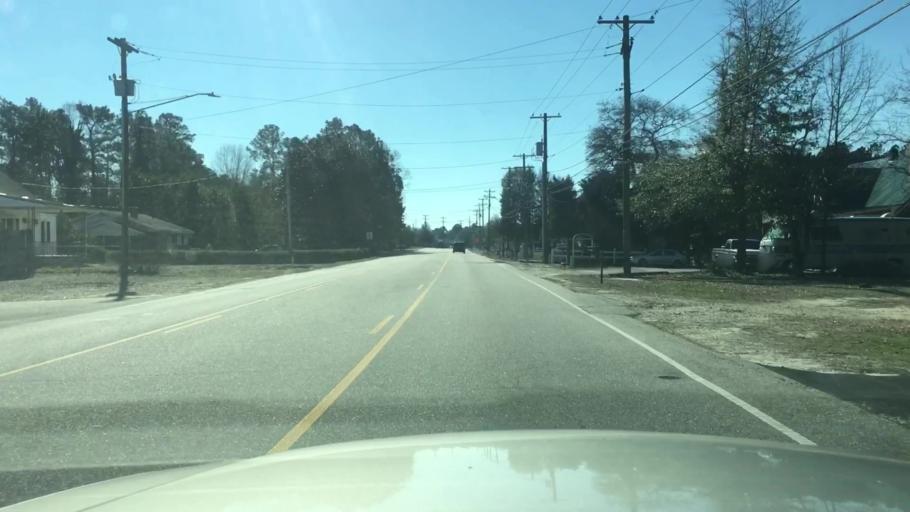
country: US
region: North Carolina
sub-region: Cumberland County
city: Hope Mills
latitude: 35.0188
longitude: -78.9353
